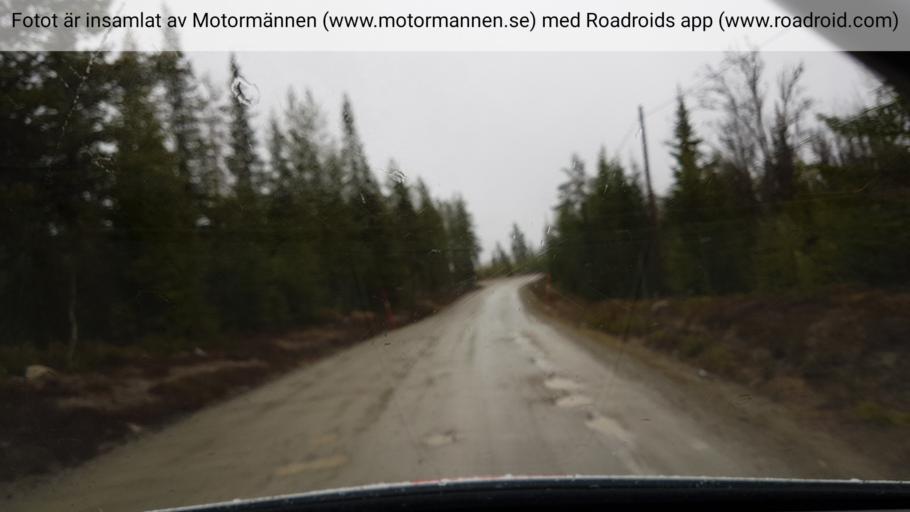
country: SE
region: Jaemtland
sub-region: Are Kommun
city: Jarpen
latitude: 62.5473
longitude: 13.4676
